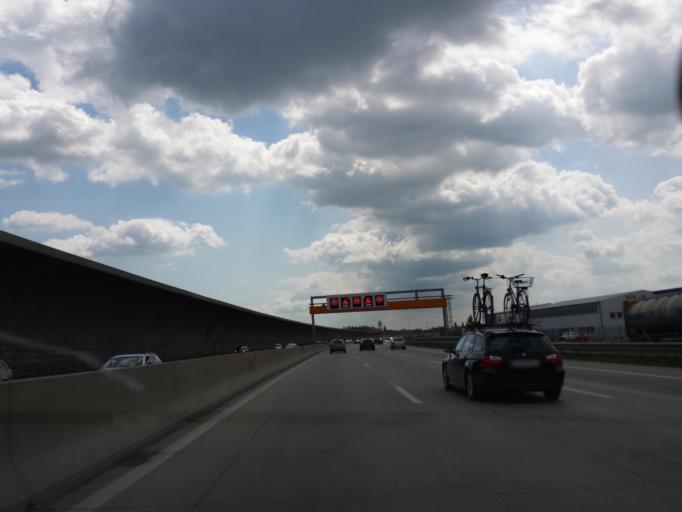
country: AT
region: Lower Austria
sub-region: Politischer Bezirk Wien-Umgebung
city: Schwechat
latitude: 48.1428
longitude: 16.5165
